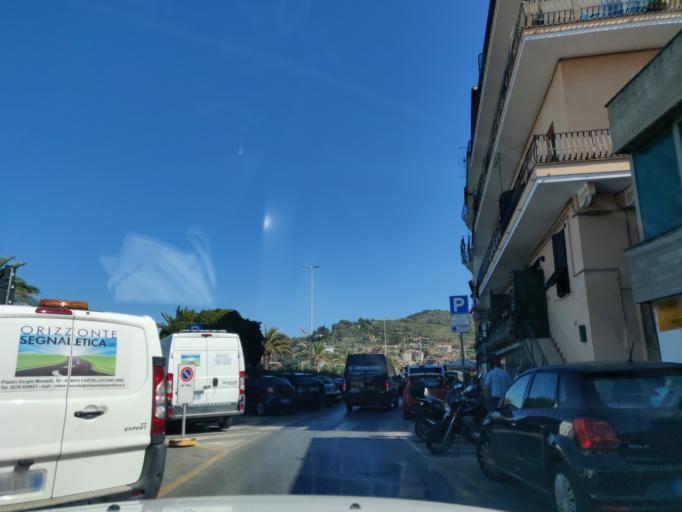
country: IT
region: Tuscany
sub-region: Provincia di Grosseto
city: Porto Santo Stefano
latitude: 42.4396
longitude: 11.1181
